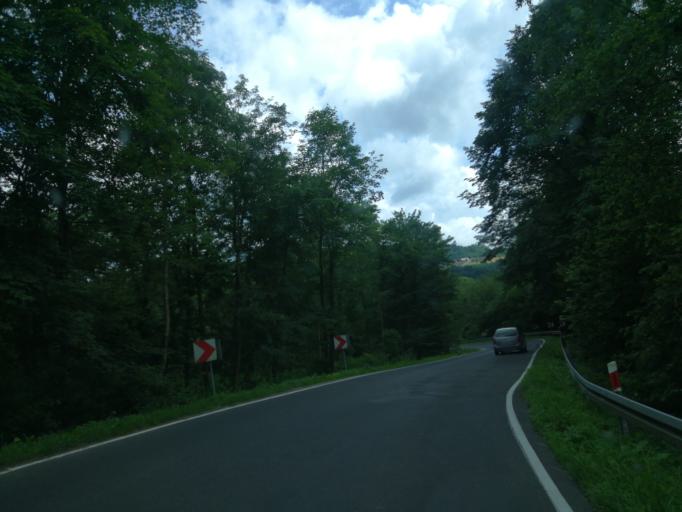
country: PL
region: Subcarpathian Voivodeship
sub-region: Powiat leski
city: Polanczyk
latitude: 49.4051
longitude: 22.4571
